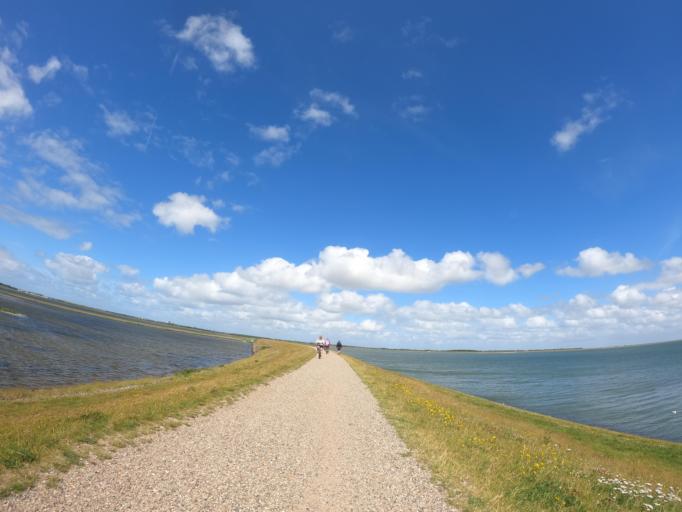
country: DE
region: Schleswig-Holstein
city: Tinnum
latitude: 54.8656
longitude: 8.3335
